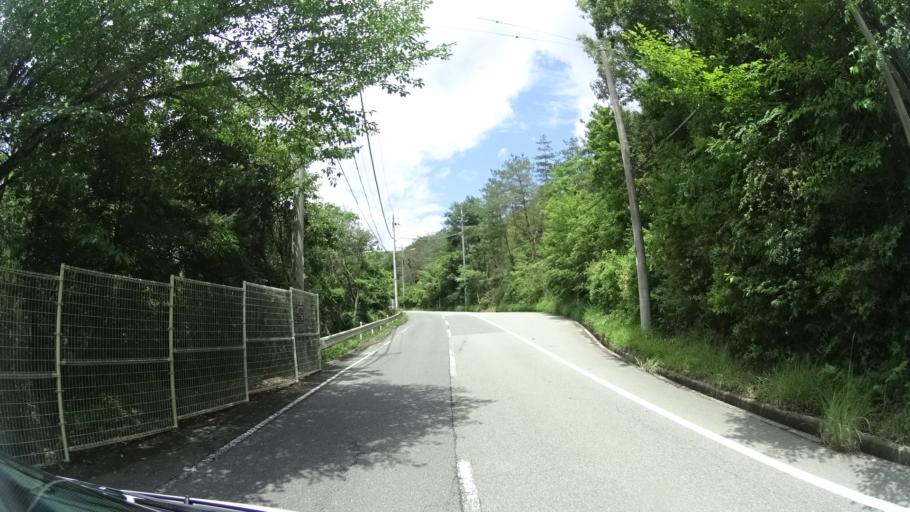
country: JP
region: Kyoto
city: Kameoka
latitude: 35.0084
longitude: 135.4669
